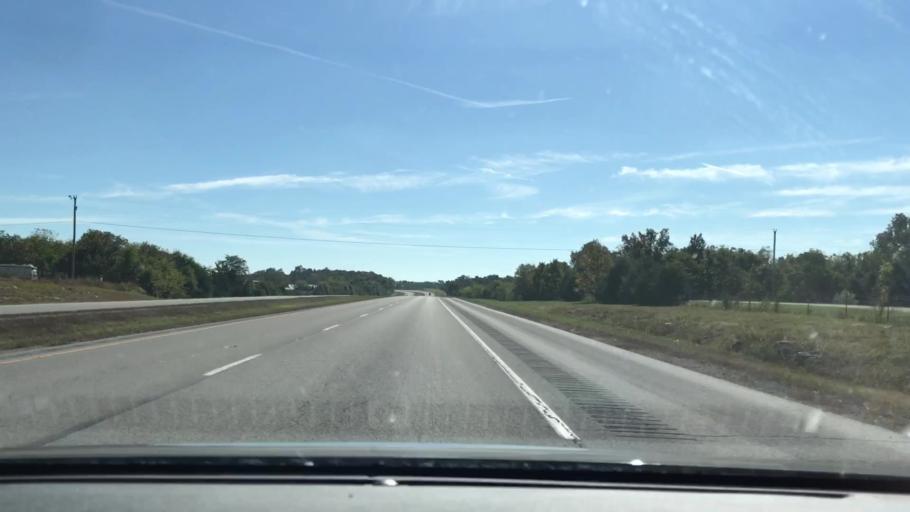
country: US
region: Kentucky
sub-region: Todd County
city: Elkton
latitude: 36.8336
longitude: -87.2330
